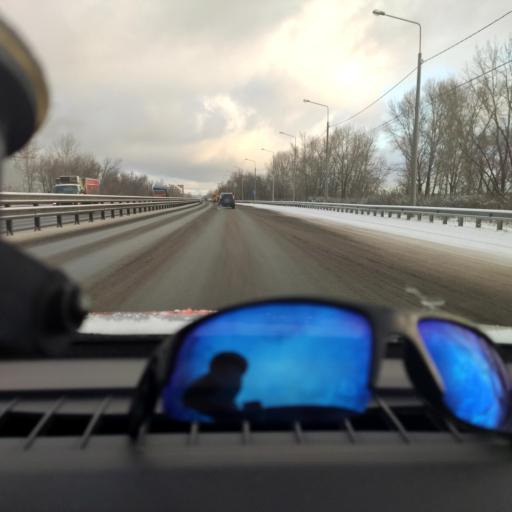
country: RU
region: Samara
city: Samara
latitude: 53.1026
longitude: 50.1608
